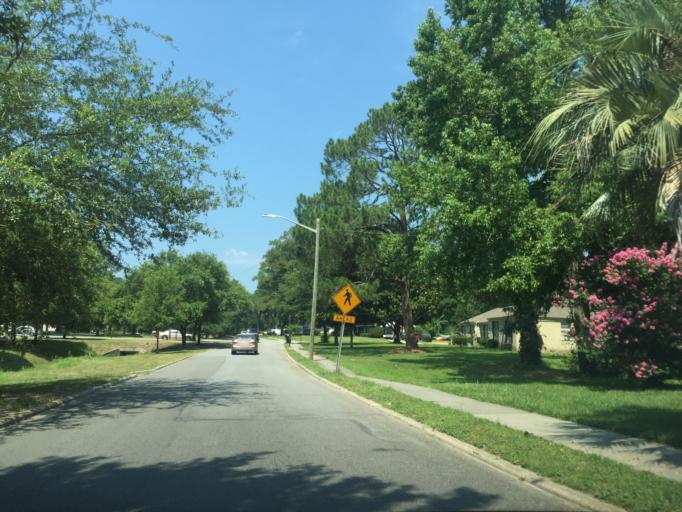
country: US
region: Georgia
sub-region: Chatham County
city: Montgomery
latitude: 31.9725
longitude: -81.1467
